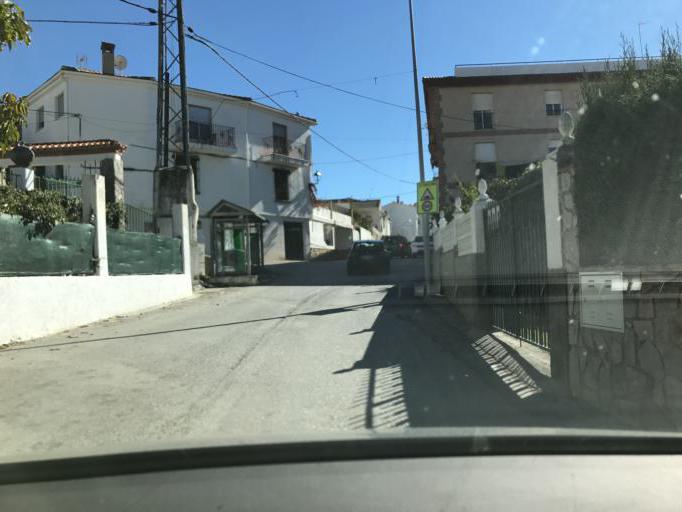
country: ES
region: Andalusia
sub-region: Provincia de Granada
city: Beas de Granada
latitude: 37.2211
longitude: -3.4815
